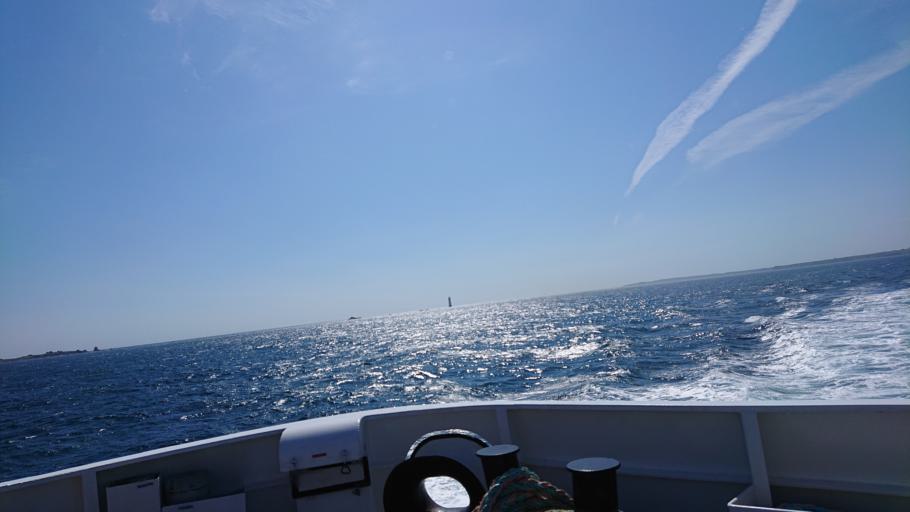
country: FR
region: Brittany
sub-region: Departement du Finistere
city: Lampaul-Plouarzel
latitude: 48.4459
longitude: -4.9964
